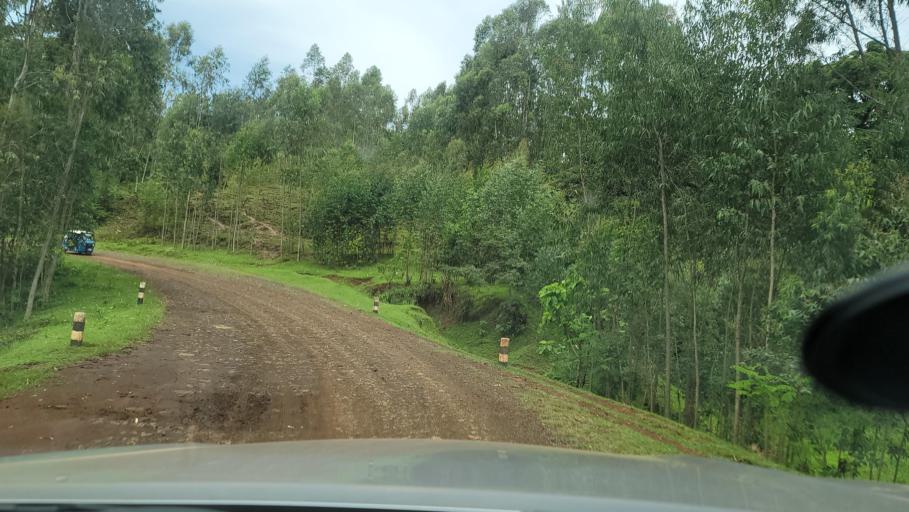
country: ET
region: Oromiya
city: Agaro
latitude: 7.7290
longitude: 36.2559
